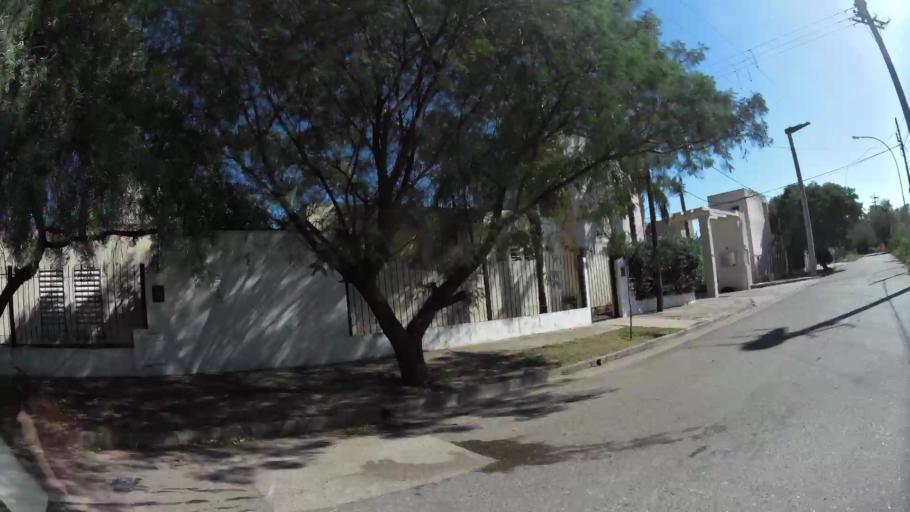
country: AR
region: Cordoba
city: Villa Allende
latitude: -31.3378
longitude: -64.2412
